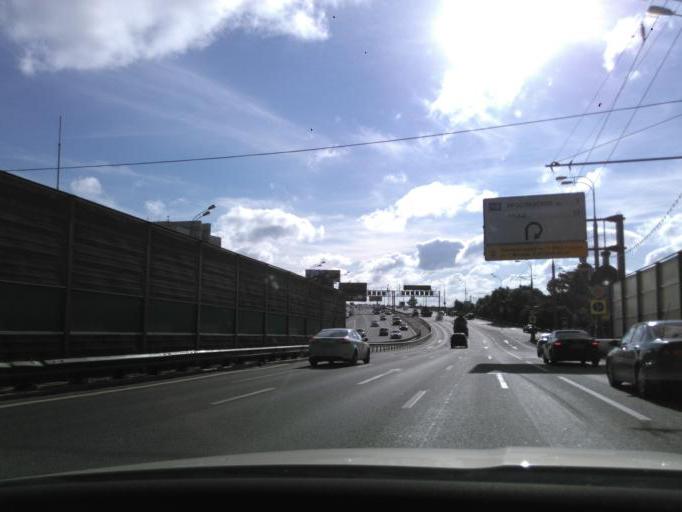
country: RU
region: Moscow
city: Mar'ina Roshcha
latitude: 55.7916
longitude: 37.6357
